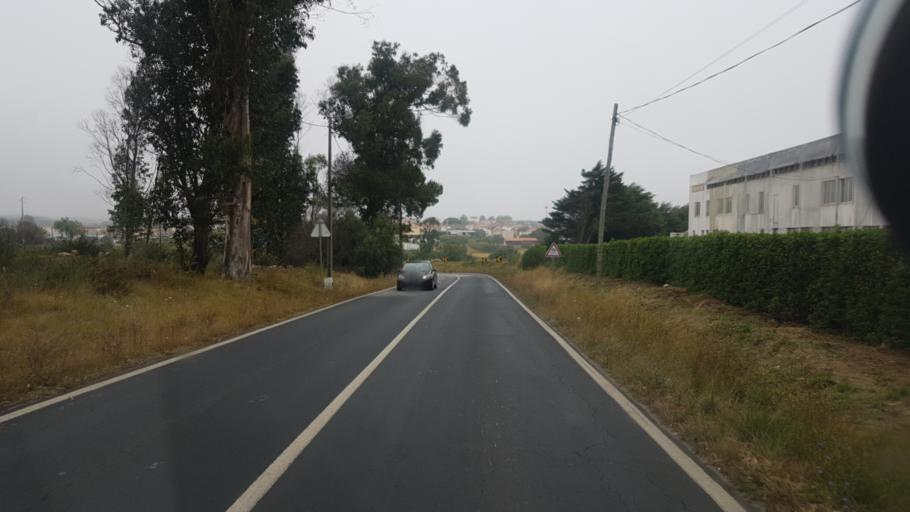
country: PT
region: Lisbon
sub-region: Sintra
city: Sintra
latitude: 38.8274
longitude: -9.3686
